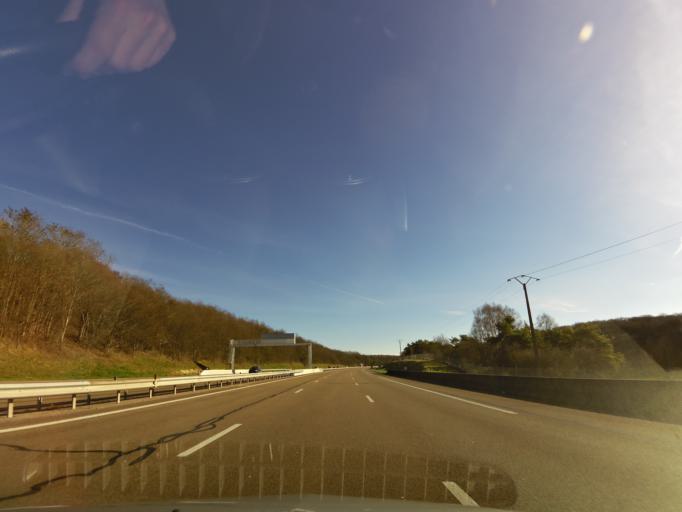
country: FR
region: Bourgogne
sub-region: Departement de l'Yonne
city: Aillant-sur-Tholon
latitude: 47.9261
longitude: 3.2746
